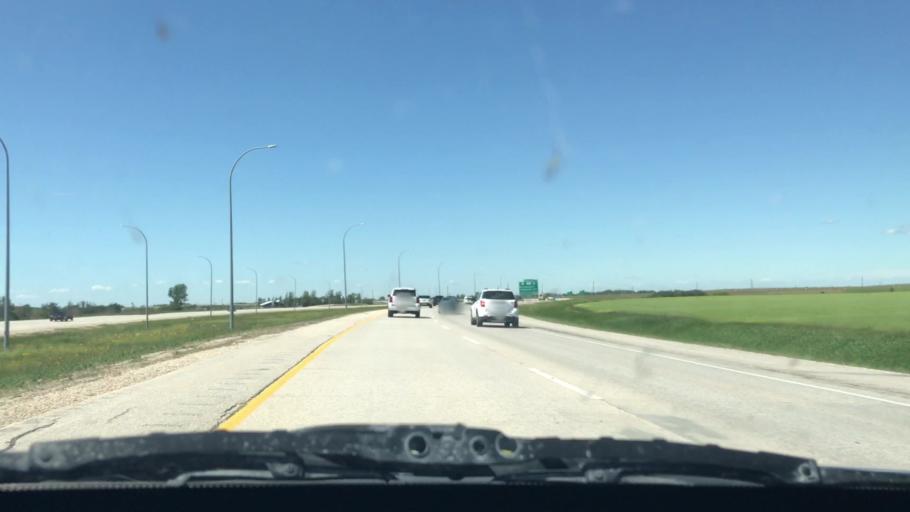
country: CA
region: Manitoba
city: Winnipeg
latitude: 49.8231
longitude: -96.9424
